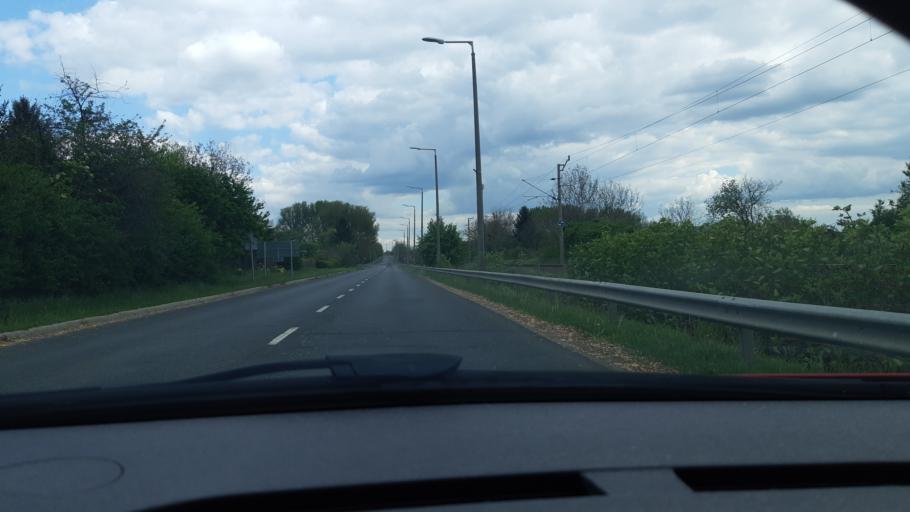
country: HU
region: Somogy
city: Kaposvar
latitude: 46.3651
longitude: 17.7672
